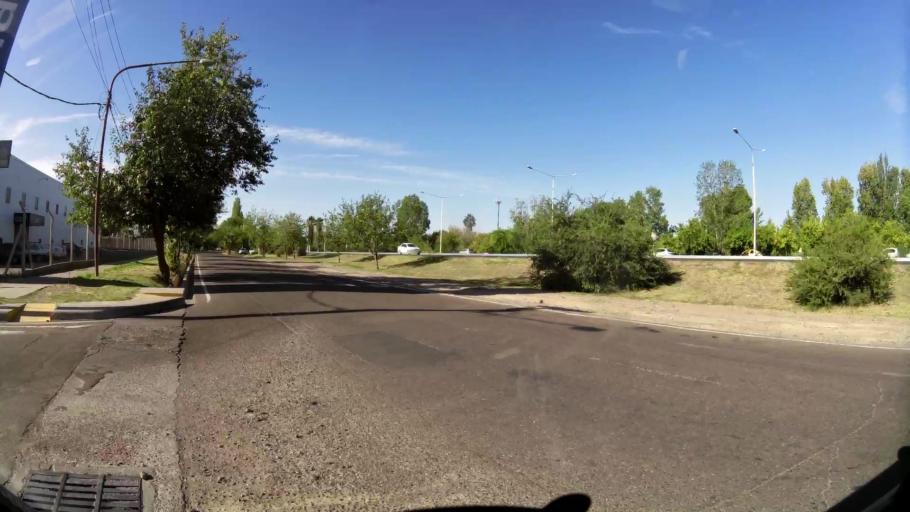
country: AR
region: Mendoza
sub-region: Departamento de Godoy Cruz
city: Godoy Cruz
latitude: -32.9143
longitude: -68.8240
